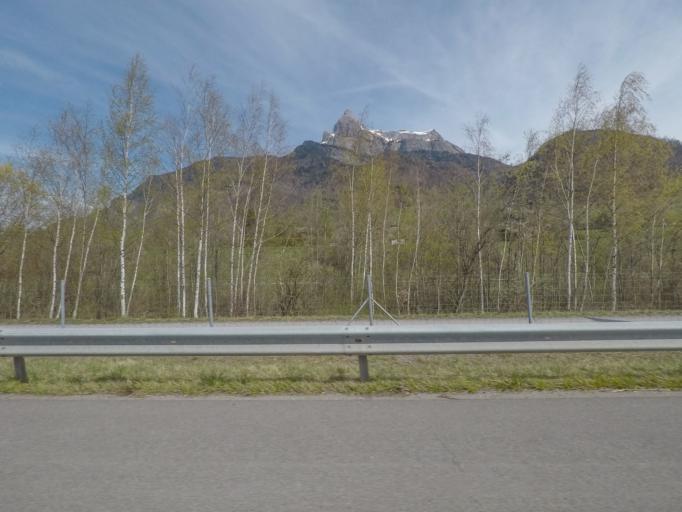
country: FR
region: Rhone-Alpes
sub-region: Departement de la Haute-Savoie
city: Domancy
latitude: 45.9242
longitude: 6.6584
